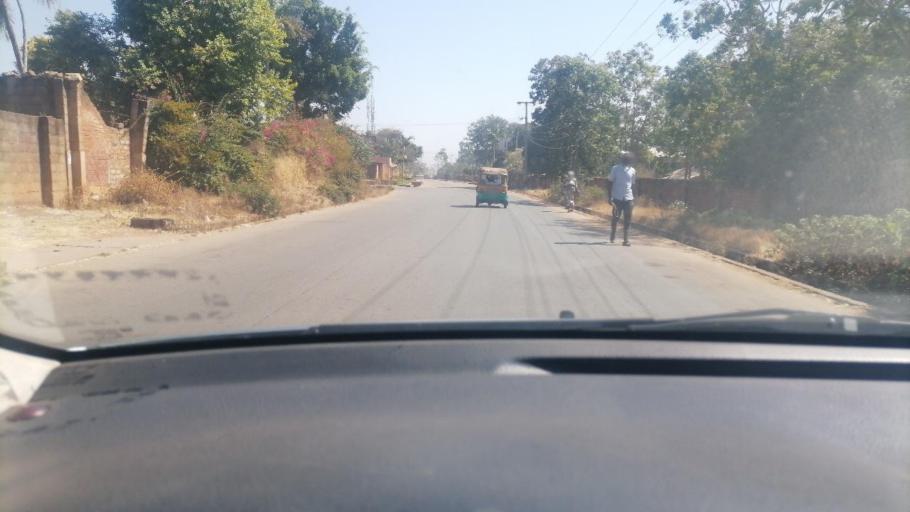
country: NG
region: Plateau
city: Jos
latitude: 9.8655
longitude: 8.9061
